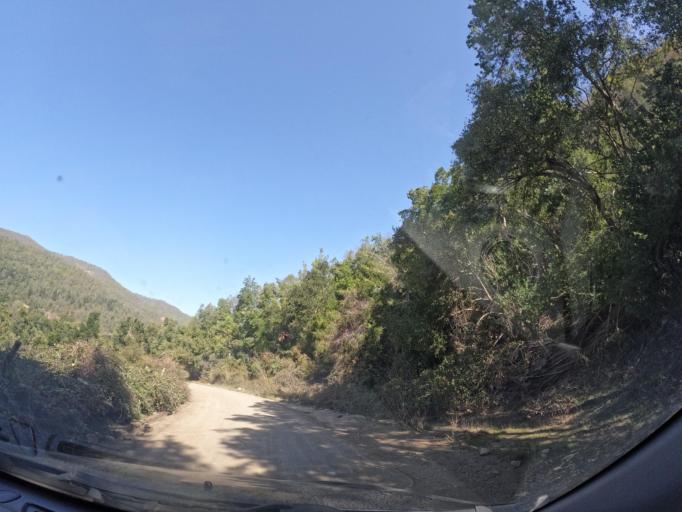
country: CL
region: Maule
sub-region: Provincia de Linares
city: Longavi
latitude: -36.2755
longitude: -71.4172
